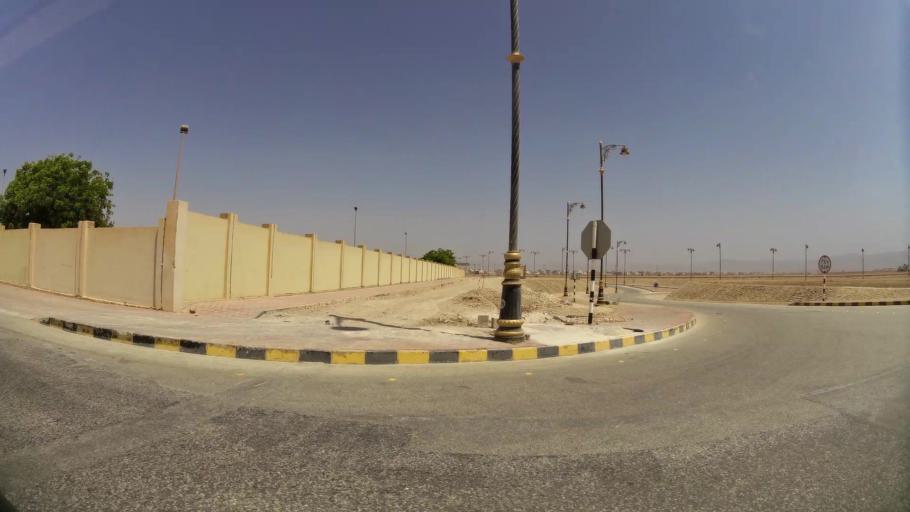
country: OM
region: Zufar
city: Salalah
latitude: 17.0492
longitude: 54.2237
